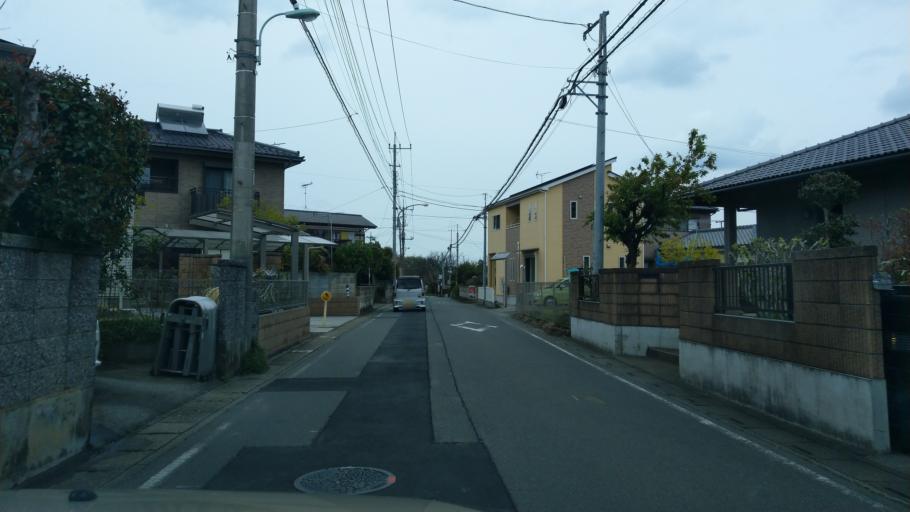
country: JP
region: Saitama
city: Ageoshimo
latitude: 35.9345
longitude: 139.5840
